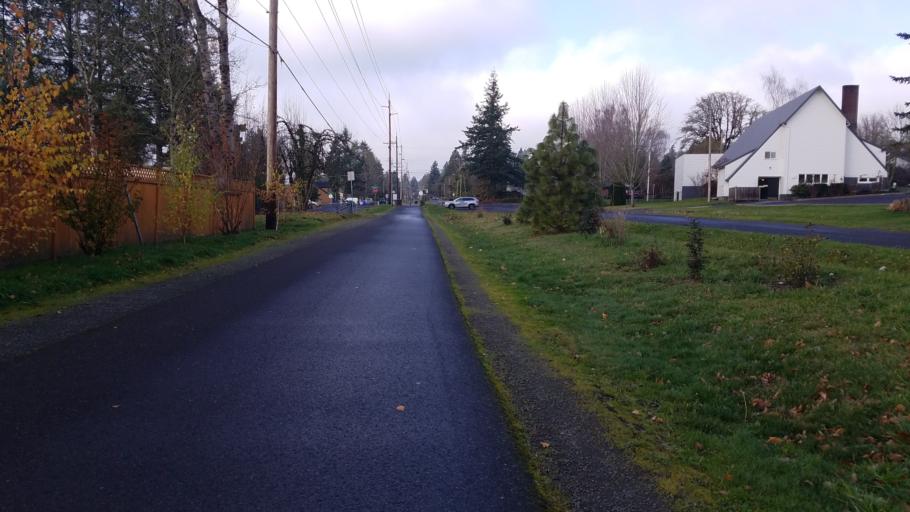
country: US
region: Oregon
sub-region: Clackamas County
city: Oak Grove
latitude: 45.4056
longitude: -122.6333
